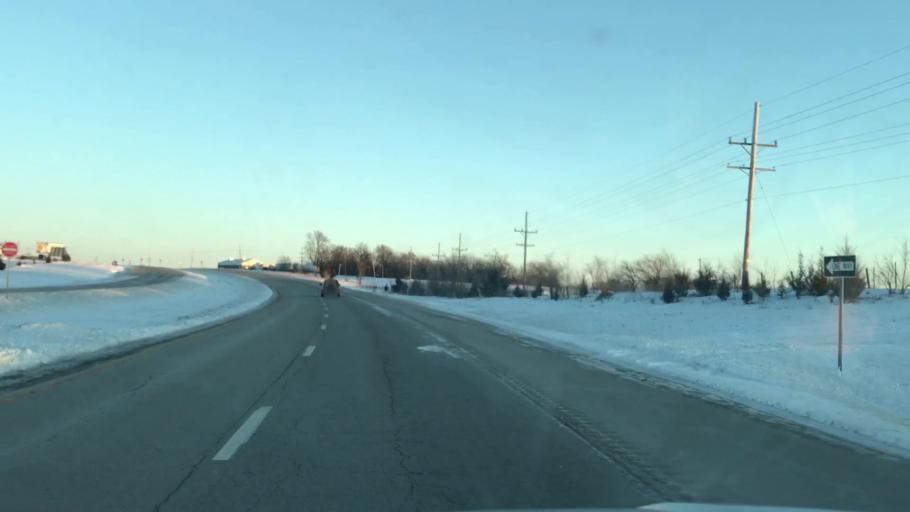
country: US
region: Missouri
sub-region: Clinton County
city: Cameron
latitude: 39.7562
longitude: -94.3424
